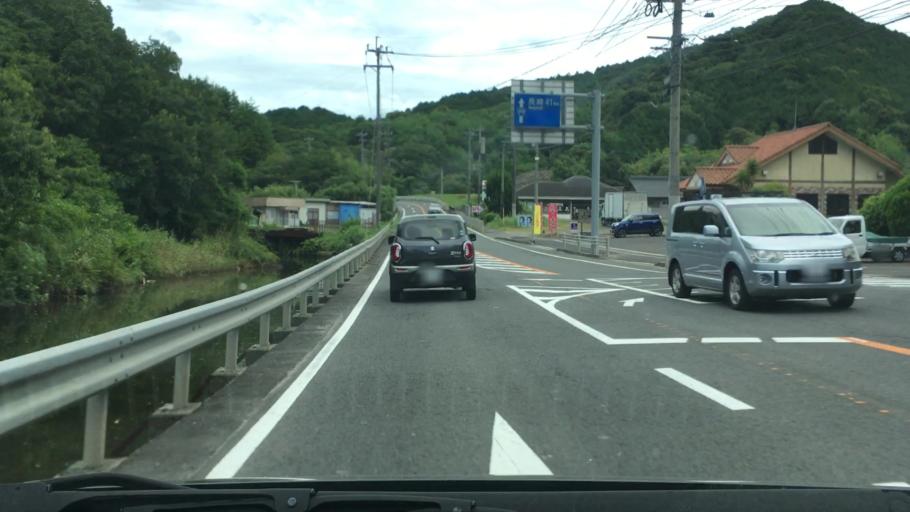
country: JP
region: Nagasaki
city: Sasebo
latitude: 32.9954
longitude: 129.7328
